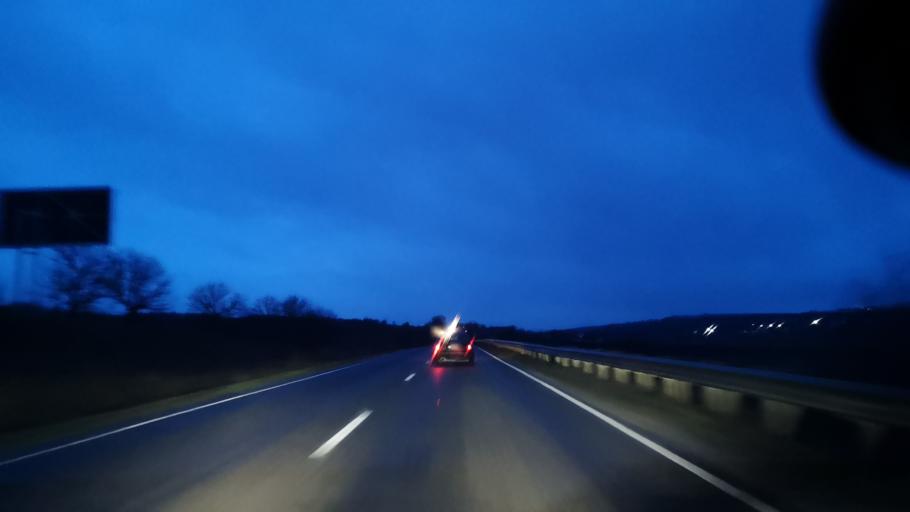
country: MD
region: Orhei
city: Orhei
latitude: 47.4090
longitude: 28.8151
